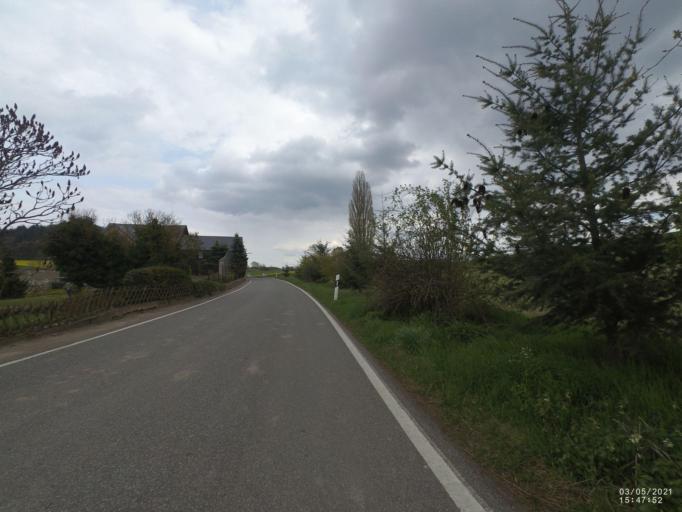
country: DE
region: Rheinland-Pfalz
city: Lonnig
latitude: 50.3423
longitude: 7.4140
